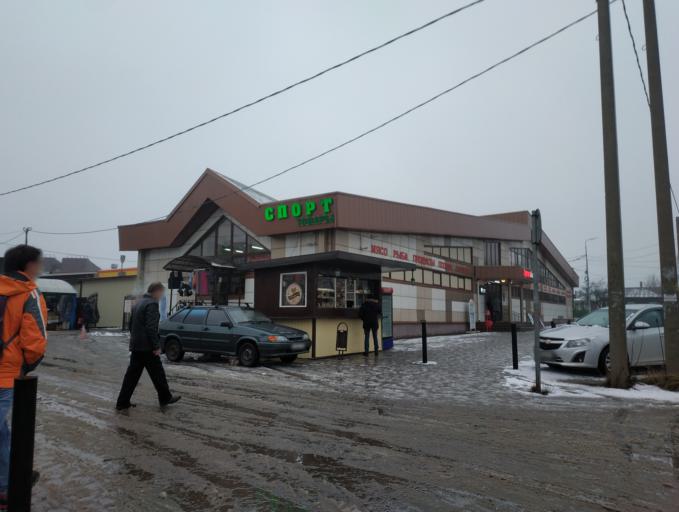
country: RU
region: Moskovskaya
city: Taldom
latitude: 56.7265
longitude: 37.5324
